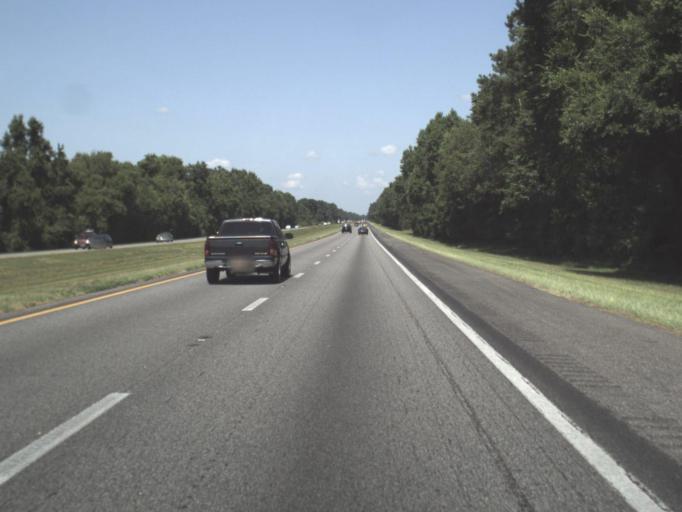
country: US
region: Florida
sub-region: Madison County
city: Madison
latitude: 30.4309
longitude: -83.5825
